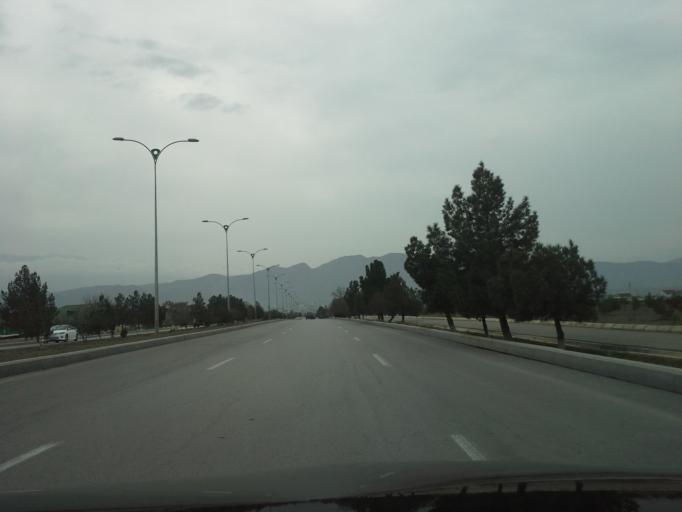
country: TM
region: Ahal
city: Abadan
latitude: 37.9720
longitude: 58.2367
